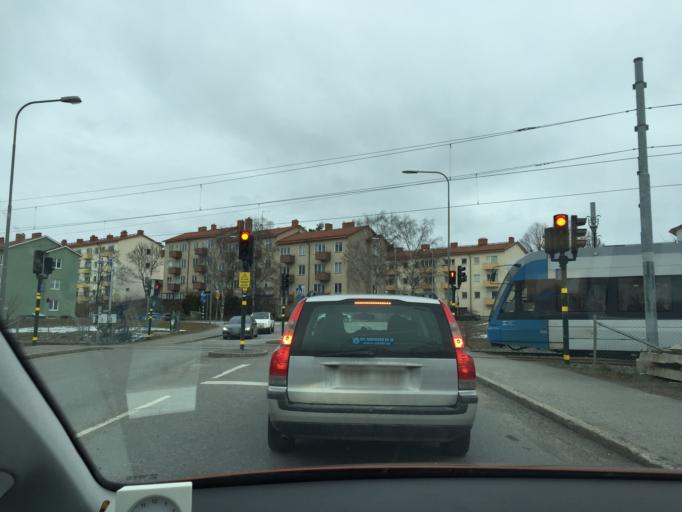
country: SE
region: Stockholm
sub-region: Stockholms Kommun
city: Arsta
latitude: 59.2960
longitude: 18.0431
